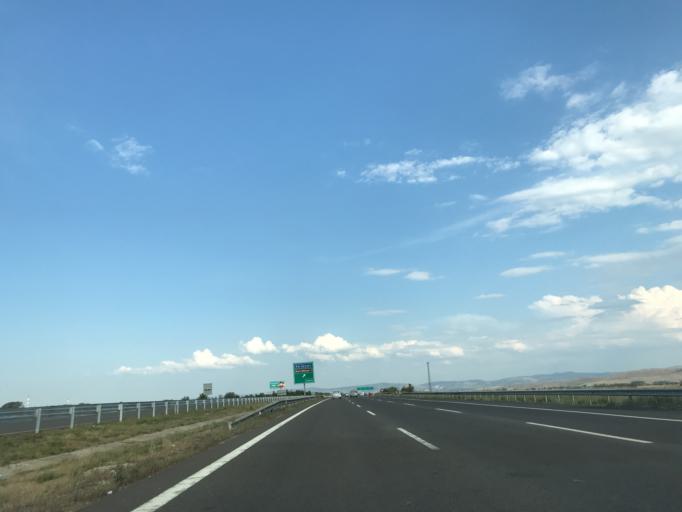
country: TR
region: Bolu
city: Dortdivan
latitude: 40.7459
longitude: 32.1059
